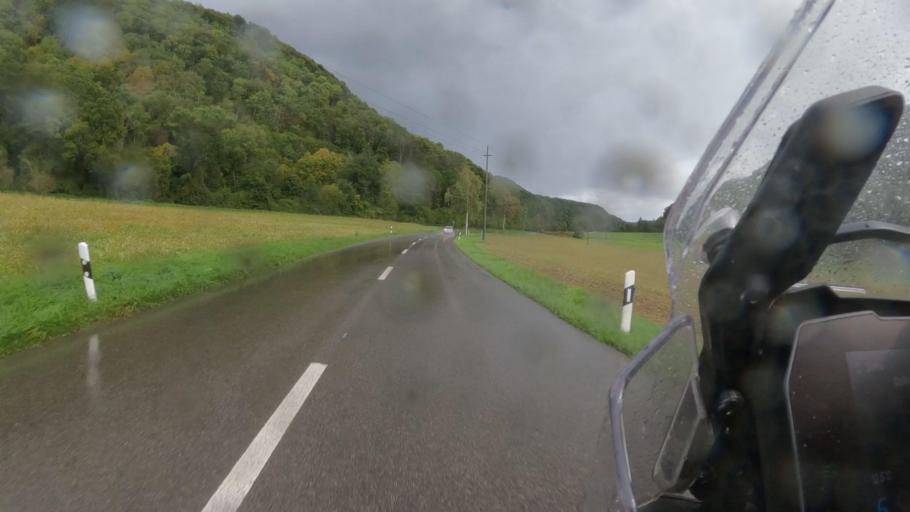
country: DE
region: Baden-Wuerttemberg
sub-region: Freiburg Region
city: Dettighofen
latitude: 47.6496
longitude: 8.5018
